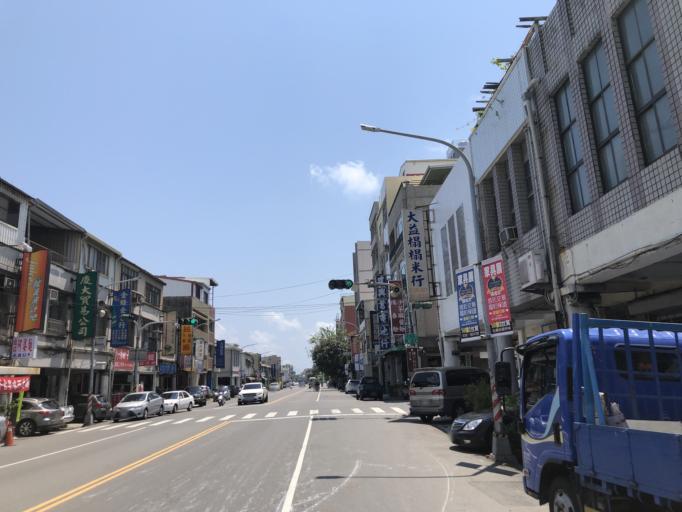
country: TW
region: Kaohsiung
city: Kaohsiung
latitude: 22.6259
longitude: 120.2778
